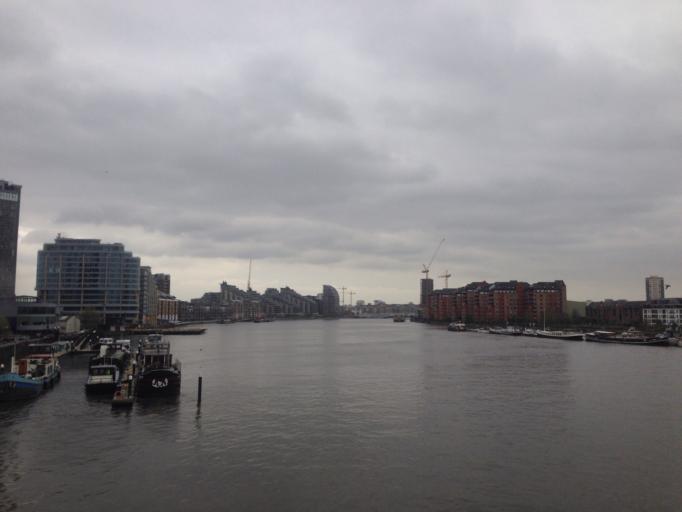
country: GB
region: England
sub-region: Greater London
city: Chelsea
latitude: 51.4727
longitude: -0.1779
